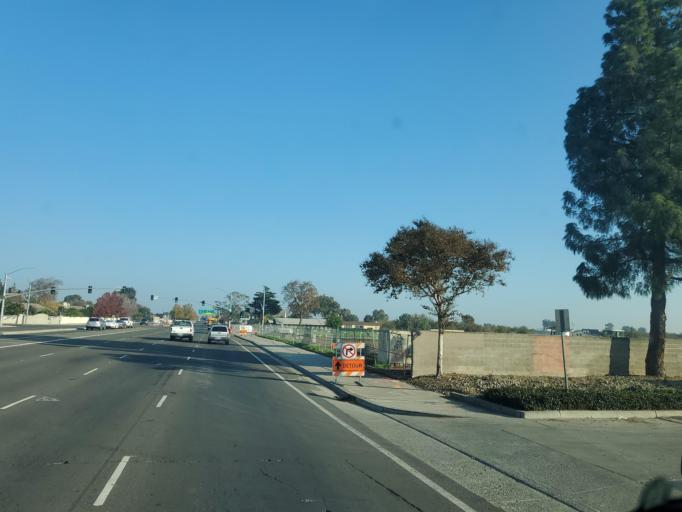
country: US
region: California
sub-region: San Joaquin County
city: Morada
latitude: 38.0210
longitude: -121.2656
